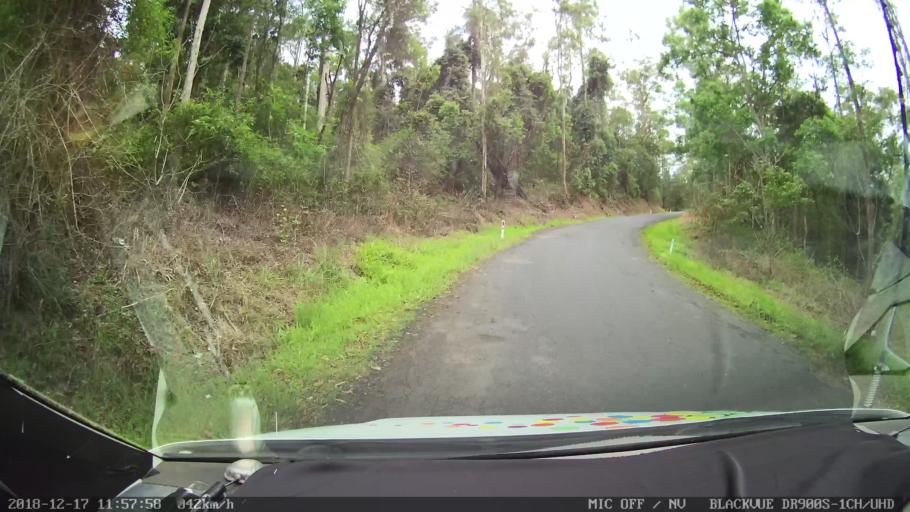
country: AU
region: New South Wales
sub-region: Kyogle
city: Kyogle
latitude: -28.5382
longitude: 152.5709
